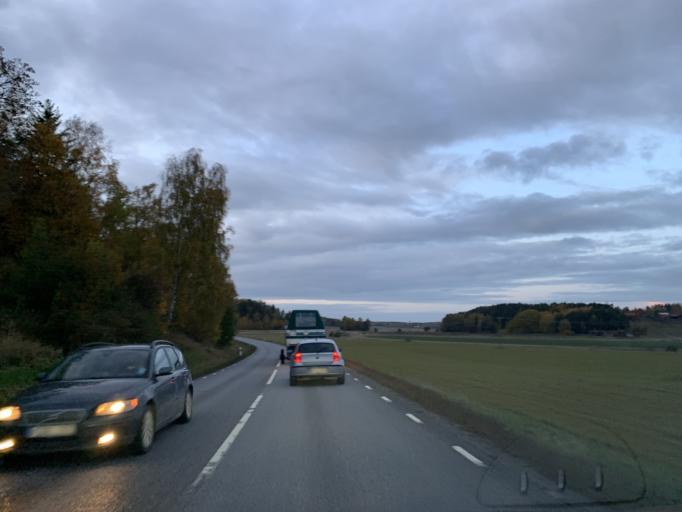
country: SE
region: Stockholm
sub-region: Nynashamns Kommun
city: Osmo
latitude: 59.0121
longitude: 17.8061
